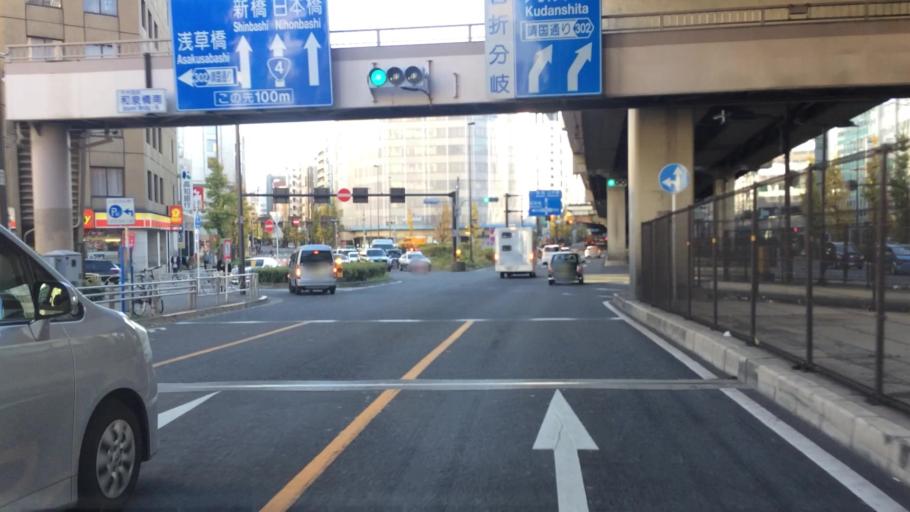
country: JP
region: Tokyo
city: Tokyo
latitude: 35.6967
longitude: 139.7756
